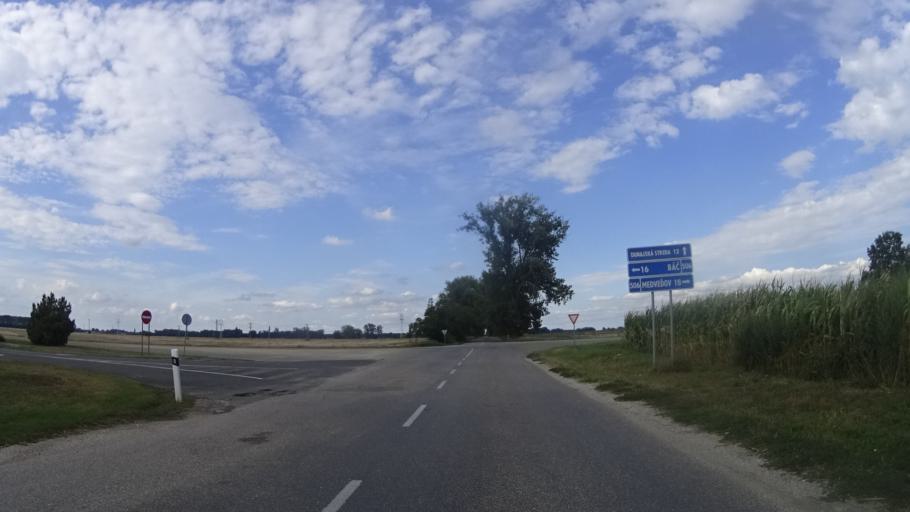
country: SK
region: Trnavsky
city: Gabcikovo
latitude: 47.9107
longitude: 17.5273
